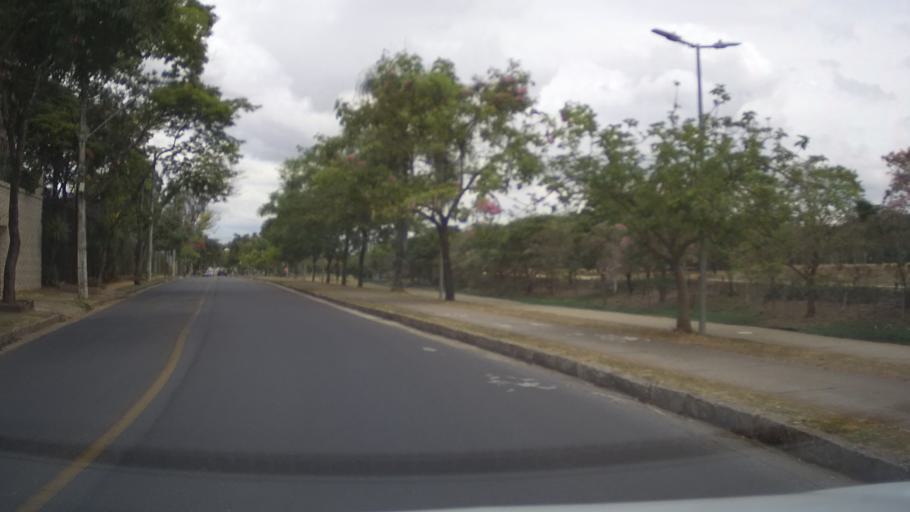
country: BR
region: Minas Gerais
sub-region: Belo Horizonte
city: Belo Horizonte
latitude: -19.8542
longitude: -43.9947
